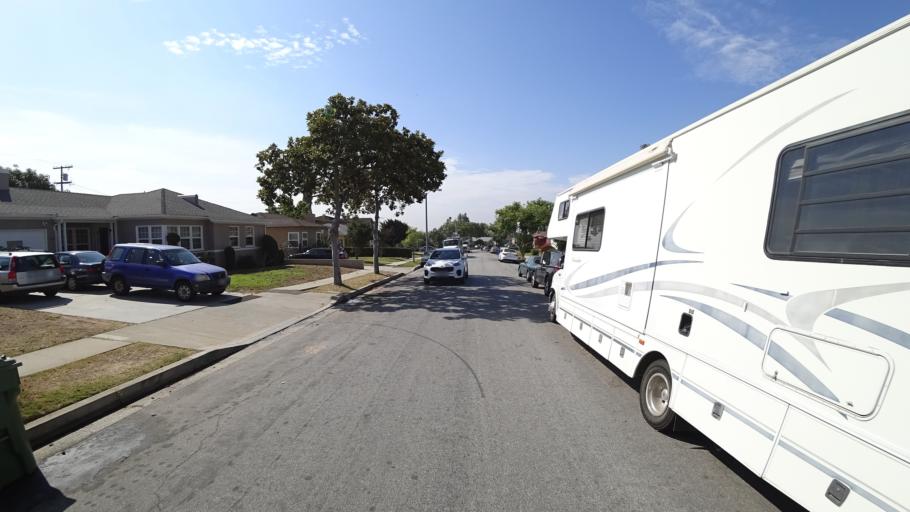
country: US
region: California
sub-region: Los Angeles County
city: View Park-Windsor Hills
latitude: 33.9907
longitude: -118.3482
